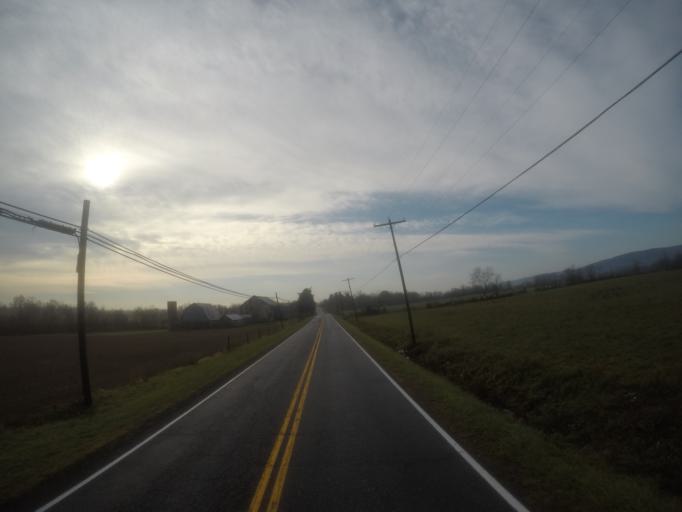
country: US
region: Maryland
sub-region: Frederick County
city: Walkersville
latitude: 39.5277
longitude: -77.4110
